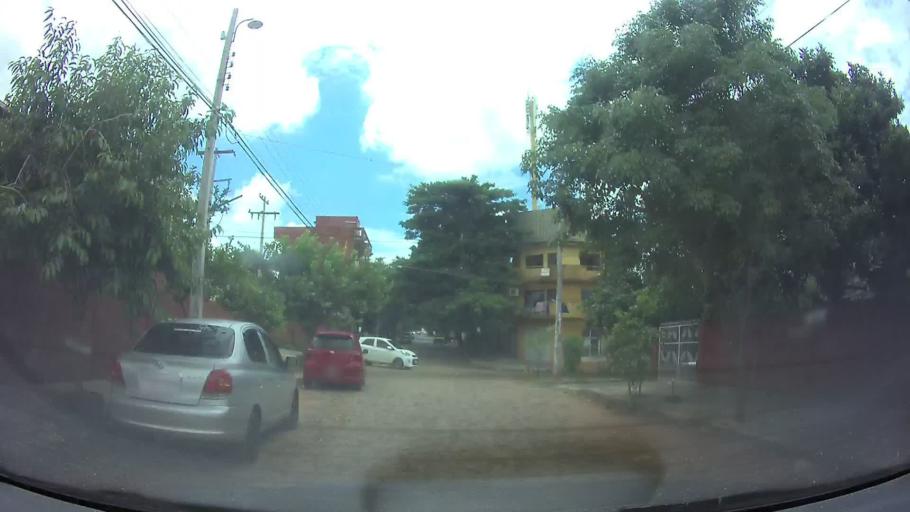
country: PY
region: Central
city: Lambare
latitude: -25.3288
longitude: -57.5830
